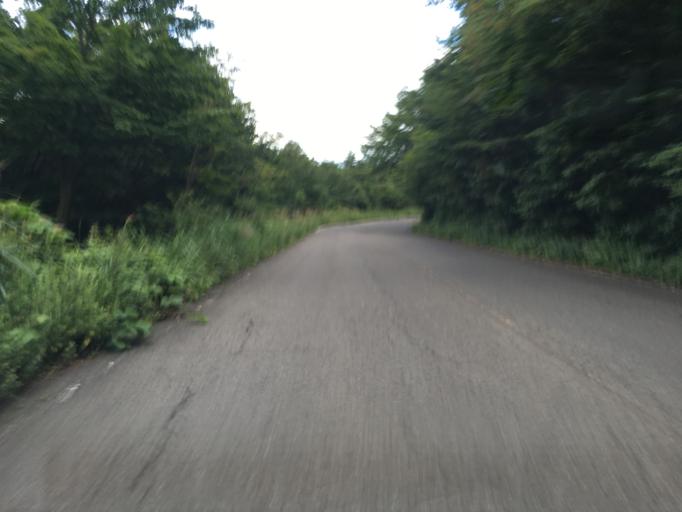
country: JP
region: Fukushima
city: Nihommatsu
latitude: 37.6224
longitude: 140.3368
